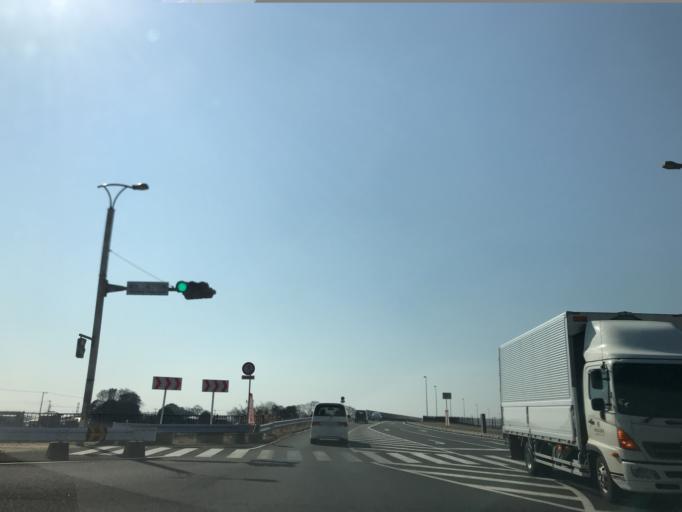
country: JP
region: Ibaraki
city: Mitsukaido
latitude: 35.9922
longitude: 140.0360
